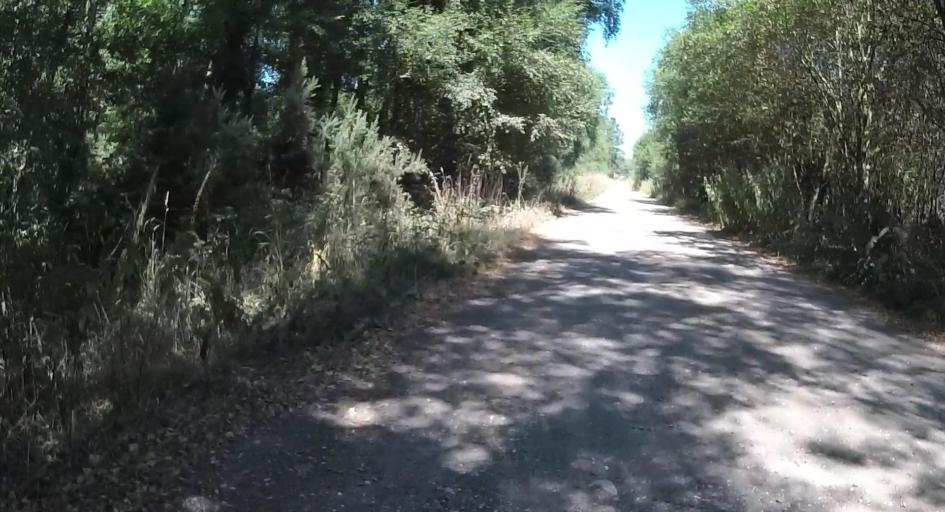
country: GB
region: England
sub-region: Dorset
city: Bovington Camp
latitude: 50.7098
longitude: -2.2694
